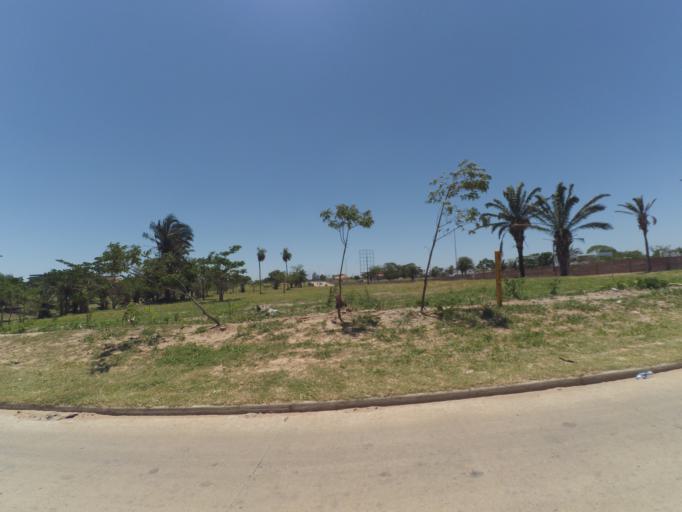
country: BO
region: Santa Cruz
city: Santa Cruz de la Sierra
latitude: -17.7549
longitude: -63.2213
